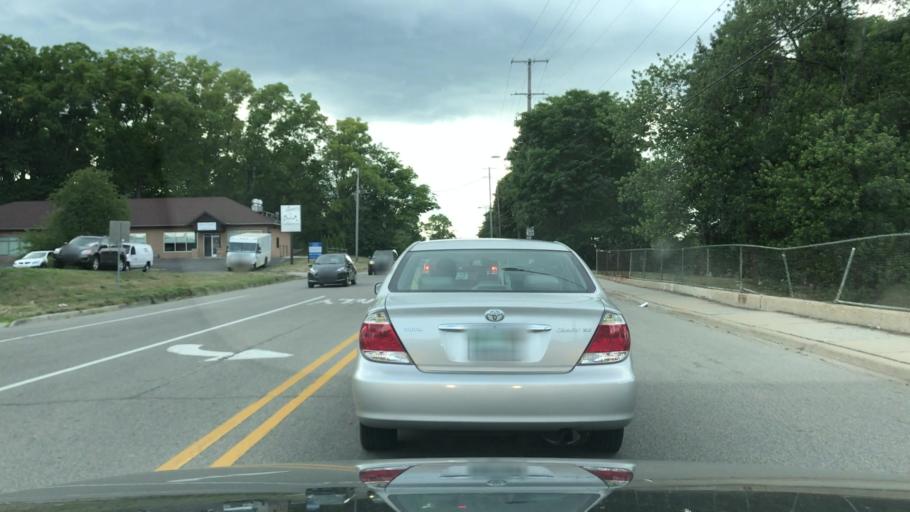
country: US
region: Michigan
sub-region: Kent County
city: Grand Rapids
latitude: 42.9990
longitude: -85.6404
